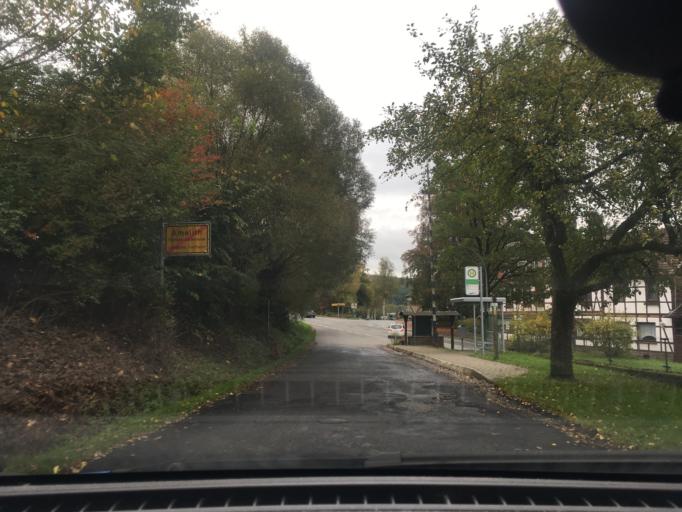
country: DE
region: Lower Saxony
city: Bodenfelde
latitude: 51.6913
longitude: 9.5169
